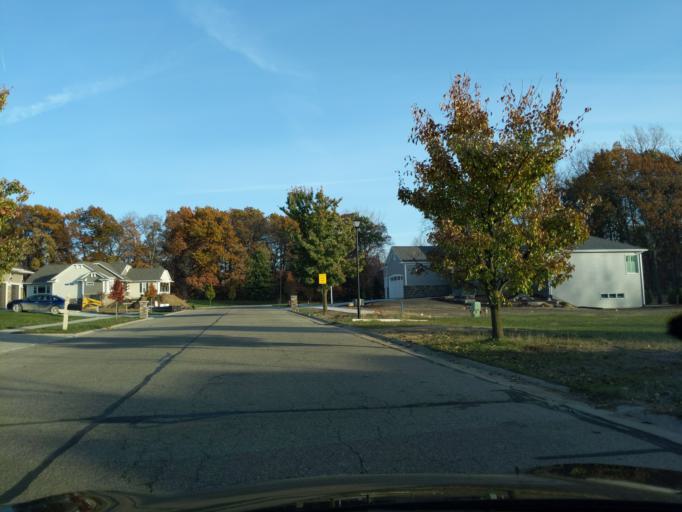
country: US
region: Michigan
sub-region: Clinton County
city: Bath
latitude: 42.7994
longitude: -84.4646
